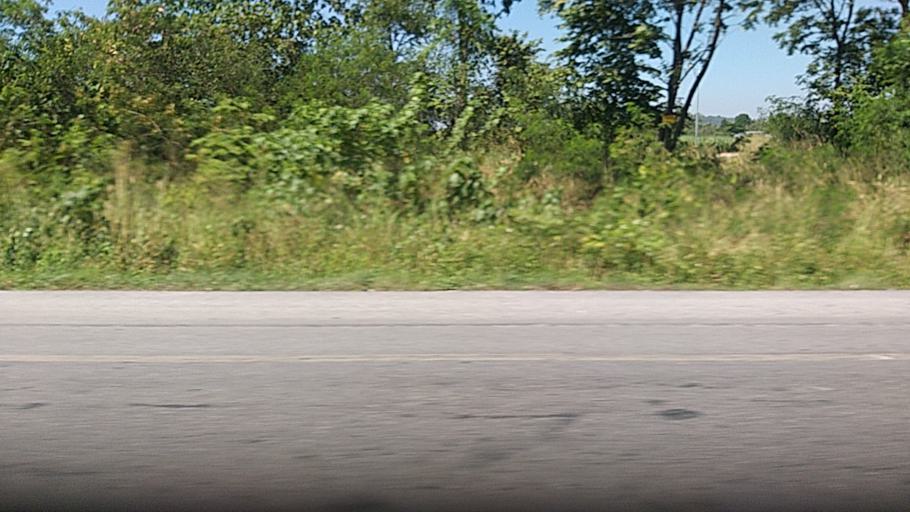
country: TH
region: Nakhon Ratchasima
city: Pak Chong
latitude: 14.7051
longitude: 101.4825
